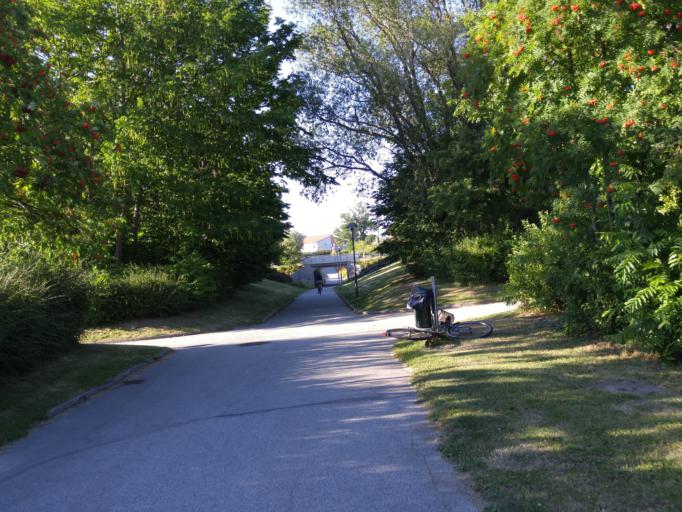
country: SE
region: Skane
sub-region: Lunds Kommun
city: Lund
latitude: 55.7273
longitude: 13.1967
